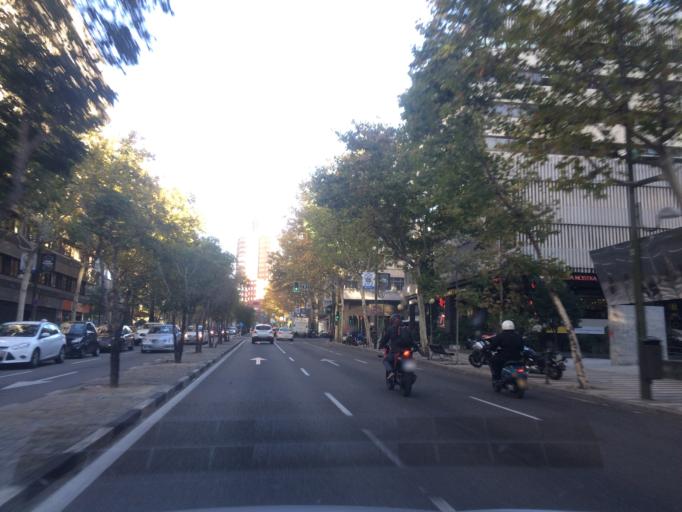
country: ES
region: Madrid
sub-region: Provincia de Madrid
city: Salamanca
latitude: 40.4376
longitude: -3.6818
